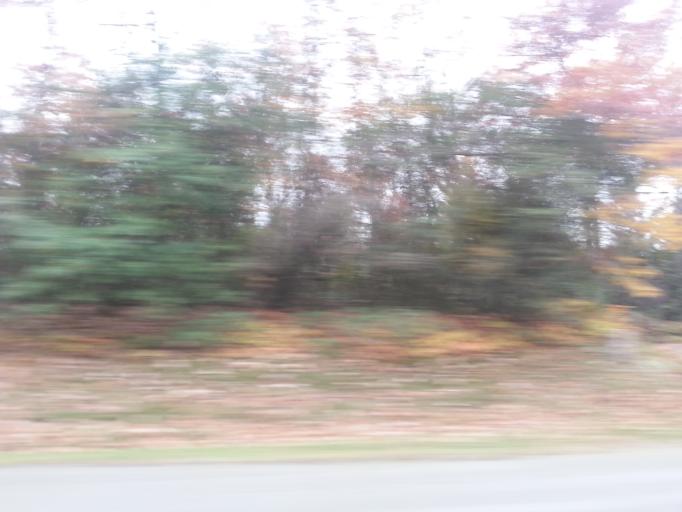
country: US
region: North Carolina
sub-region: Ashe County
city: West Jefferson
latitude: 36.2835
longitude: -81.3881
